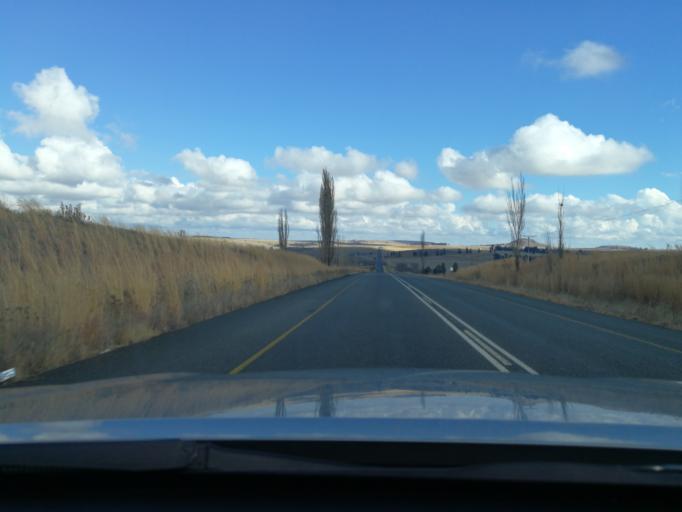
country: ZA
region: Orange Free State
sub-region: Thabo Mofutsanyana District Municipality
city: Reitz
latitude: -27.9352
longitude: 28.3864
